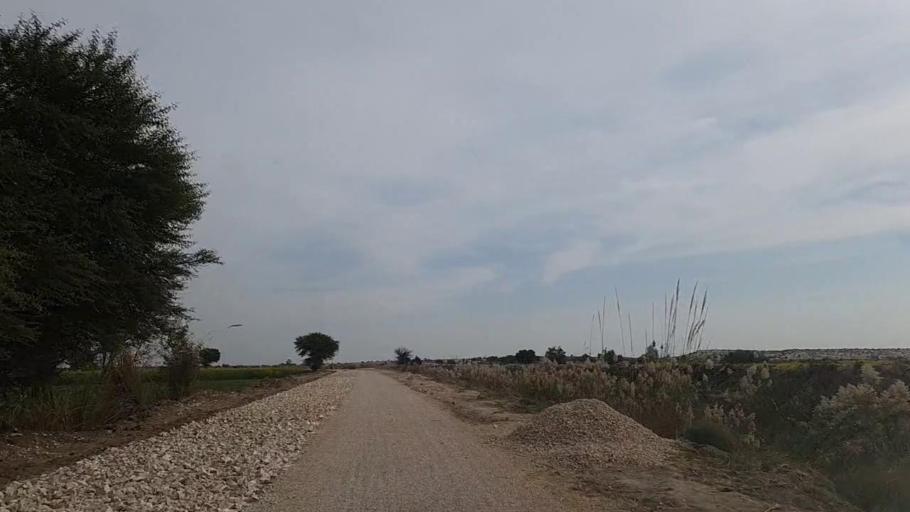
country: PK
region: Sindh
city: Jam Sahib
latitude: 26.4052
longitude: 68.4952
